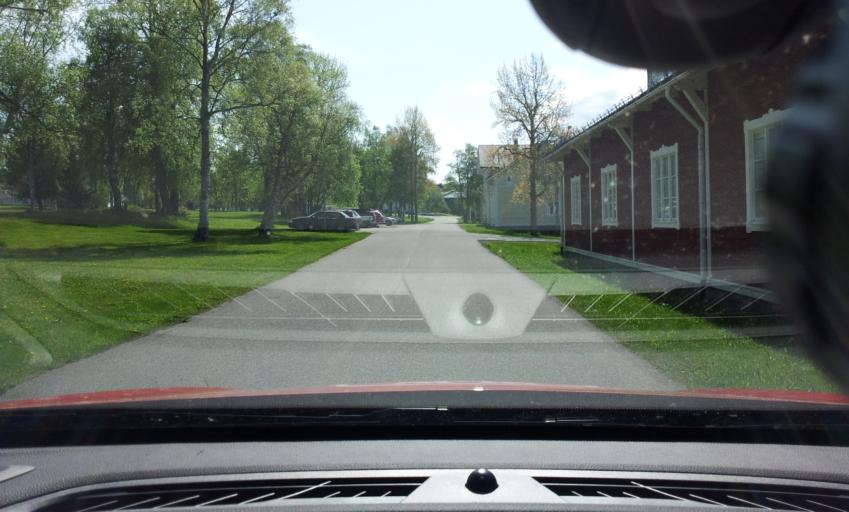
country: SE
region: Jaemtland
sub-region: Krokoms Kommun
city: Krokom
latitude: 63.1948
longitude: 14.4803
